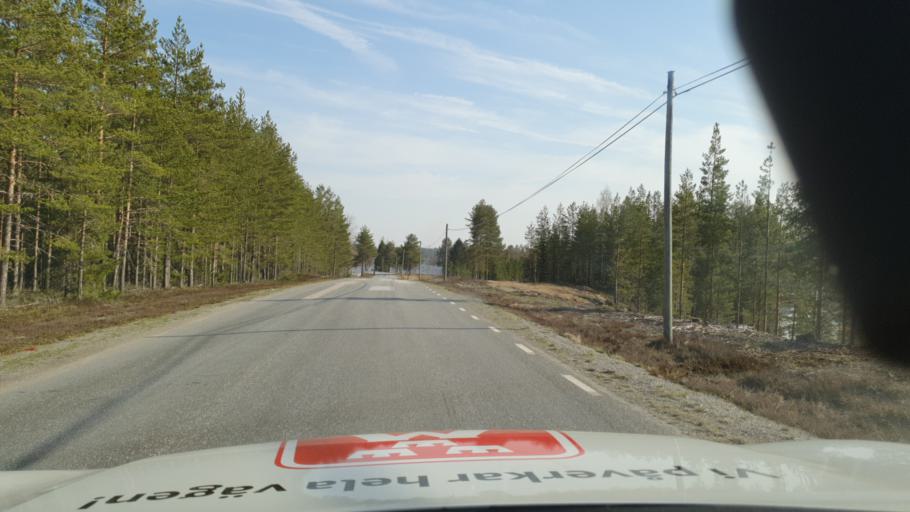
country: SE
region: Vaesterbotten
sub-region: Umea Kommun
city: Roback
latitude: 63.9144
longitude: 20.1443
